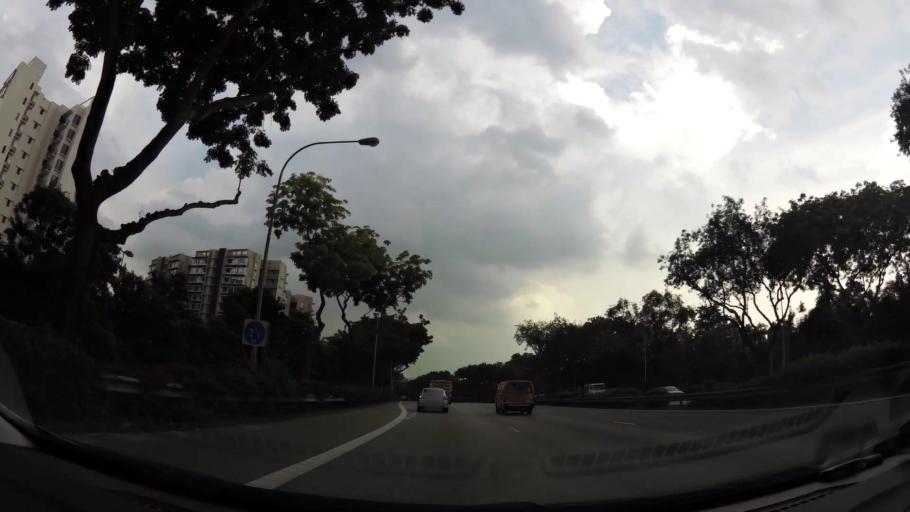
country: MY
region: Johor
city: Kampung Pasir Gudang Baru
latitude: 1.3691
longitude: 103.9433
